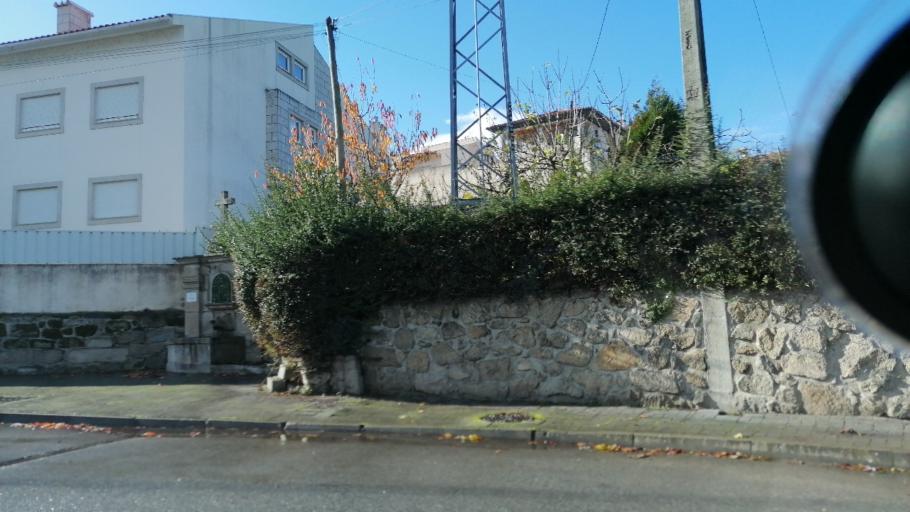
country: PT
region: Viseu
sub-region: Lamego
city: Lamego
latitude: 41.1049
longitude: -7.7948
